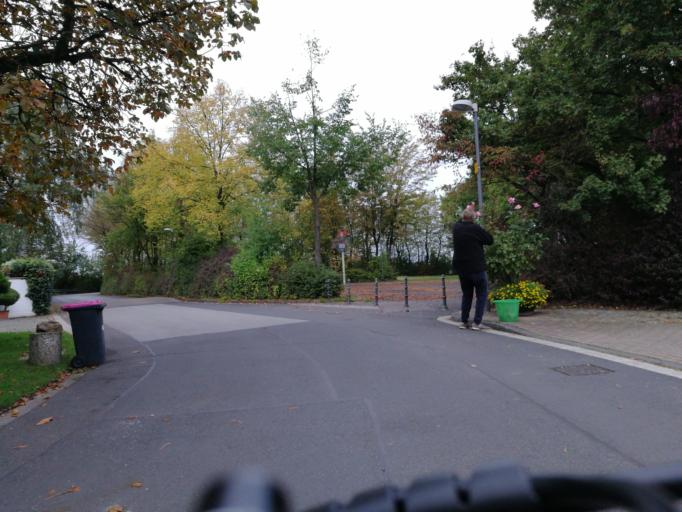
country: DE
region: North Rhine-Westphalia
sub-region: Regierungsbezirk Dusseldorf
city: Dusseldorf
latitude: 51.1490
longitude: 6.7490
